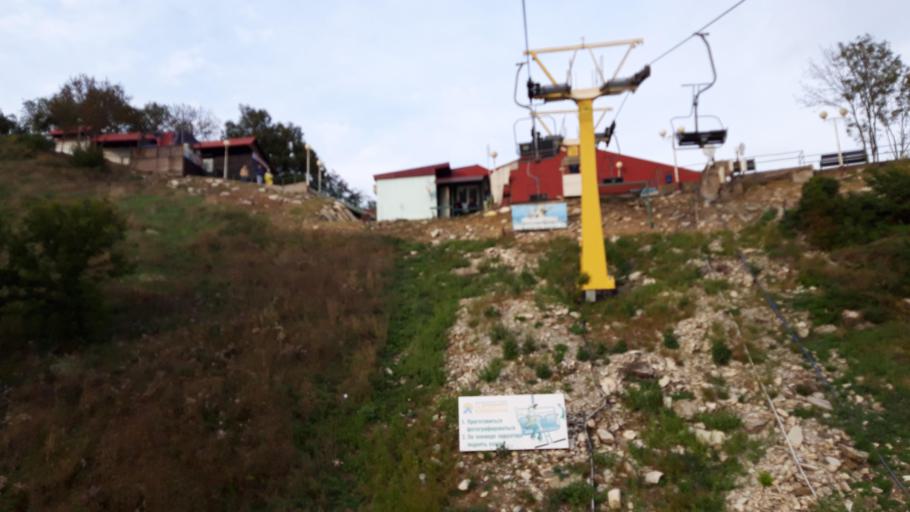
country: RU
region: Krasnodarskiy
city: Gelendzhik
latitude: 44.5848
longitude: 38.1012
